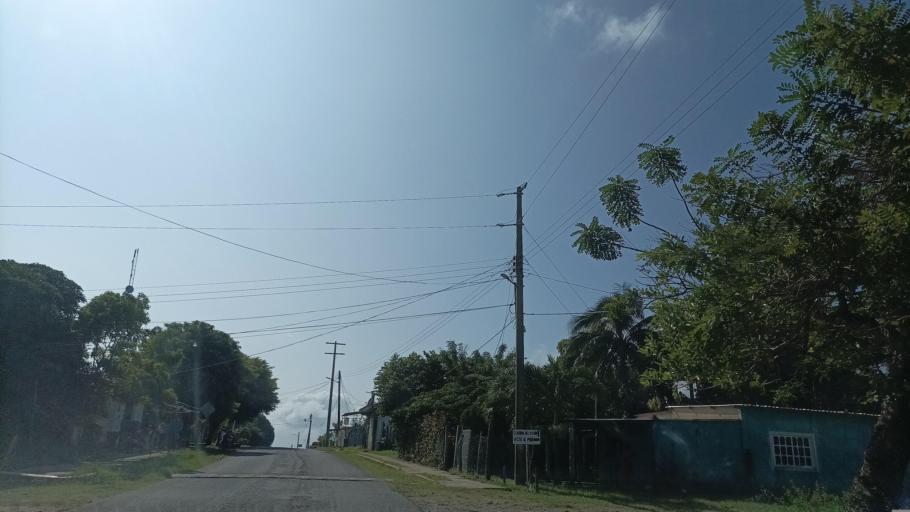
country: MX
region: Veracruz
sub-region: Coatzacoalcos
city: Fraccionamiento Ciudad Olmeca
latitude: 18.2151
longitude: -94.6140
